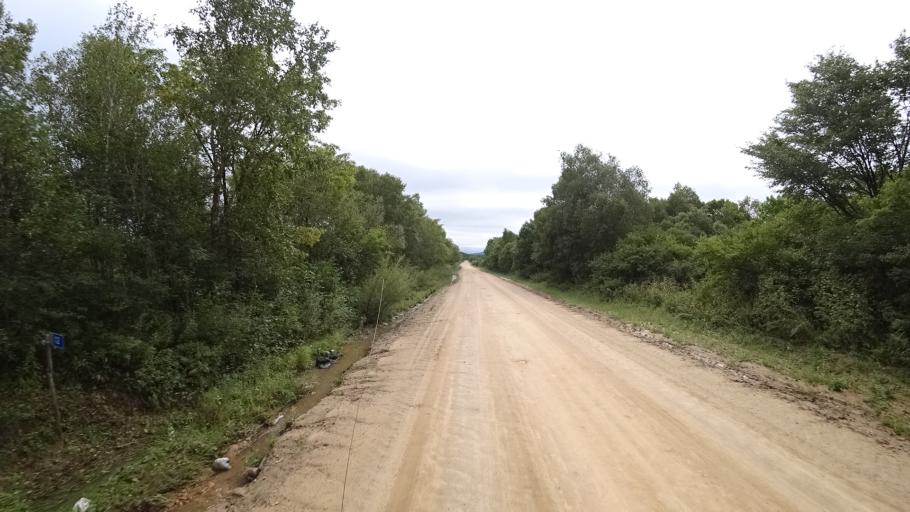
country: RU
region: Primorskiy
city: Monastyrishche
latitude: 44.1066
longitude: 132.6138
